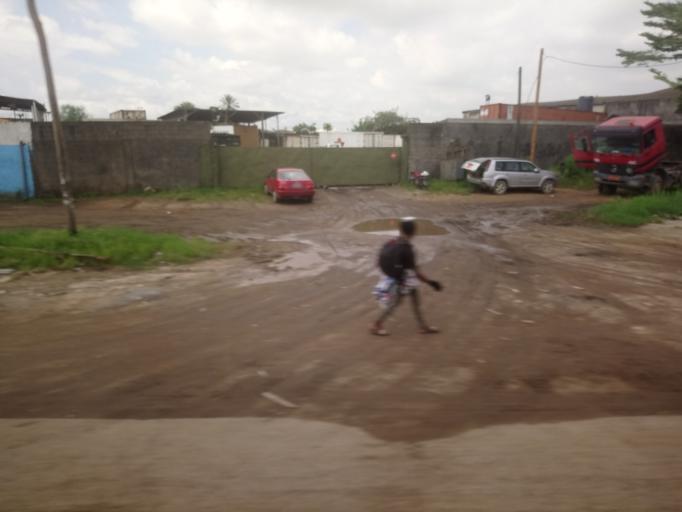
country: CM
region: Littoral
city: Douala
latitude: 4.0238
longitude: 9.7204
